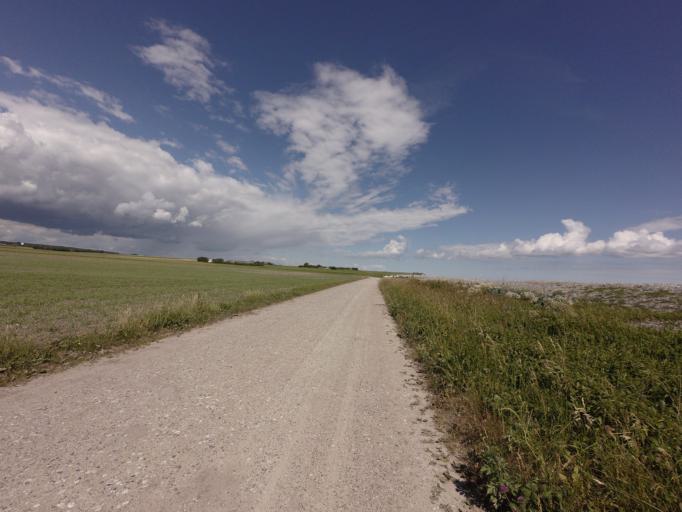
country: DK
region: Central Jutland
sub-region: Norddjurs Kommune
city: Grenaa
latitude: 56.4932
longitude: 10.8714
